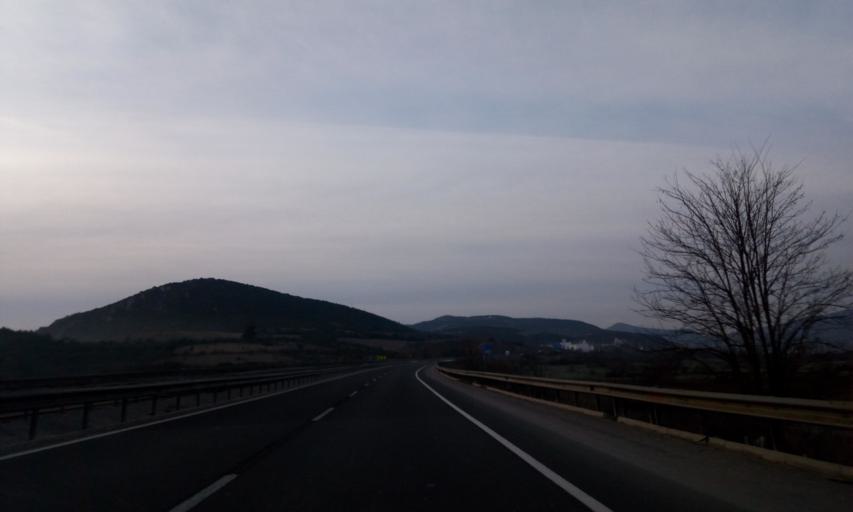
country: TR
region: Bilecik
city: Bilecik
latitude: 40.1436
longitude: 30.0264
